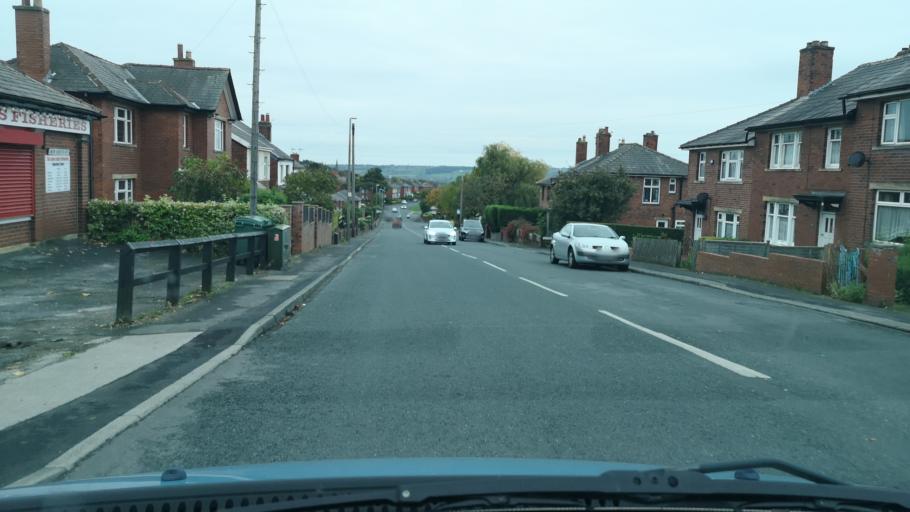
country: GB
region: England
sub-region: Kirklees
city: Heckmondwike
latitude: 53.7153
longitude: -1.6792
